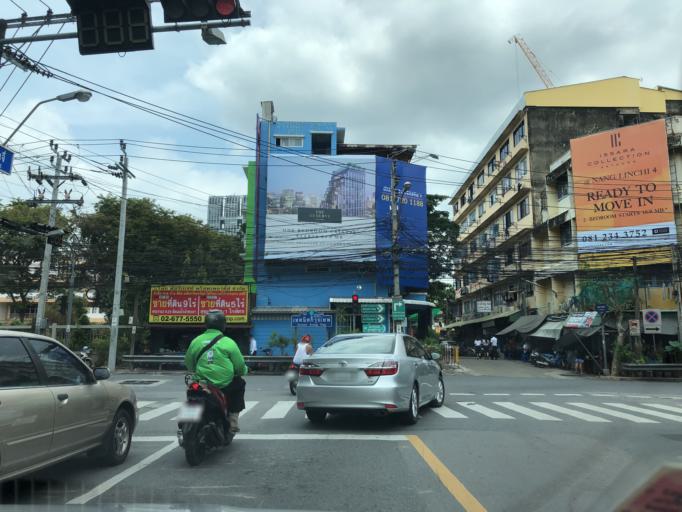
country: TH
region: Bangkok
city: Sathon
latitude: 13.7159
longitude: 100.5389
